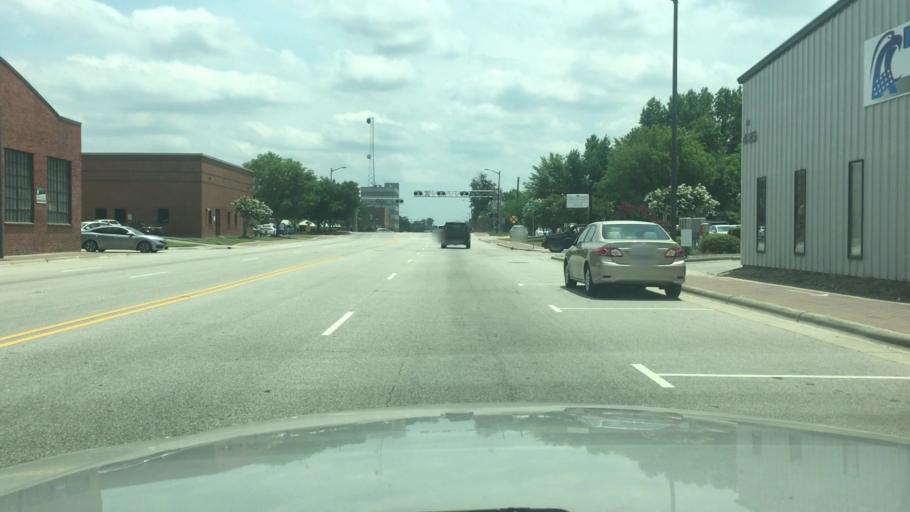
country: US
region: North Carolina
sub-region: Cumberland County
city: Fayetteville
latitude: 35.0524
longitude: -78.8848
